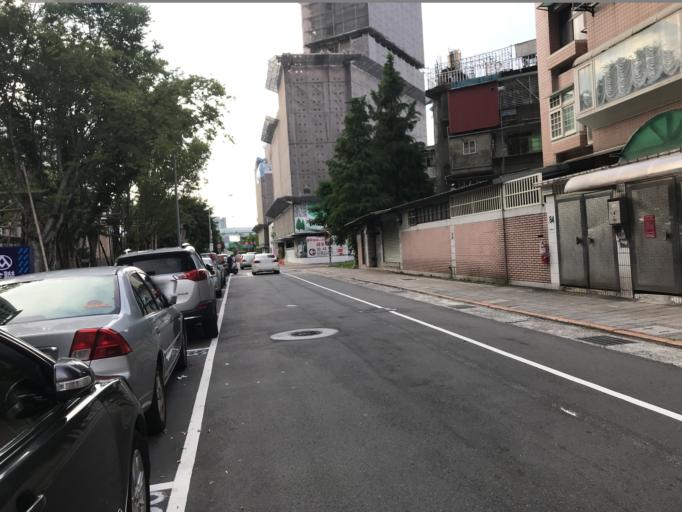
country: TW
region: Taipei
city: Taipei
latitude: 24.9973
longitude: 121.5386
